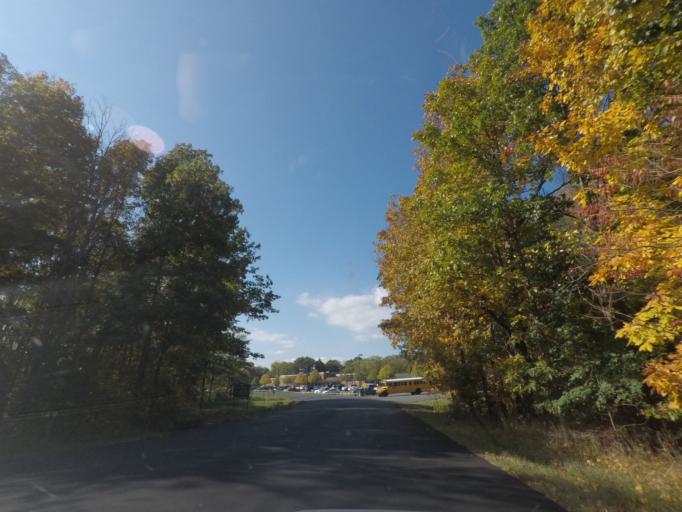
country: US
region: New York
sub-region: Rensselaer County
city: Averill Park
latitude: 42.6438
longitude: -73.5704
